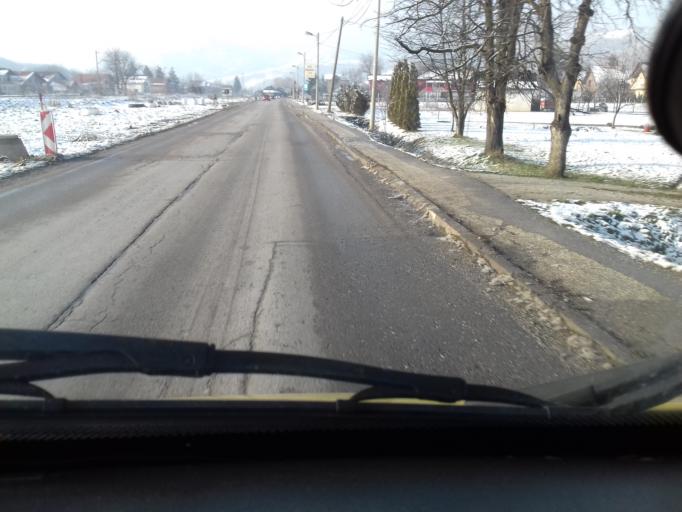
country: BA
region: Federation of Bosnia and Herzegovina
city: Mahala
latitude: 43.9868
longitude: 18.2351
